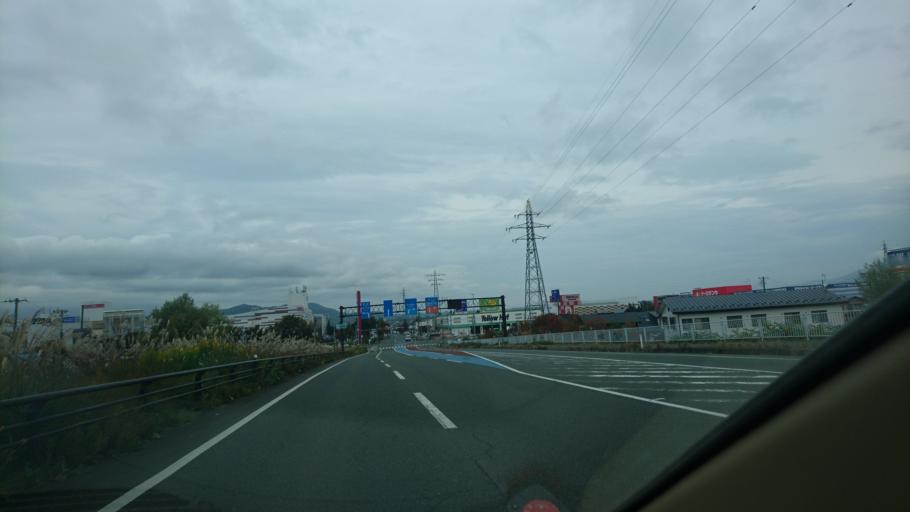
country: JP
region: Iwate
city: Morioka-shi
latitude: 39.7086
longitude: 141.1014
